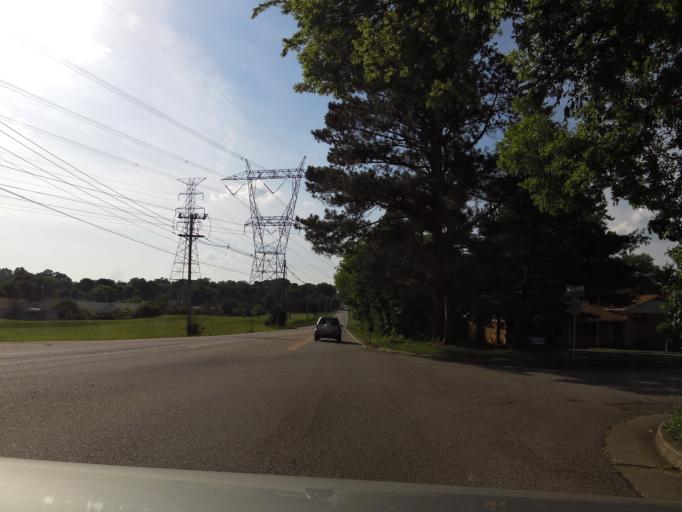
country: US
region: Tennessee
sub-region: Blount County
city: Alcoa
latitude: 35.7867
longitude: -84.0078
